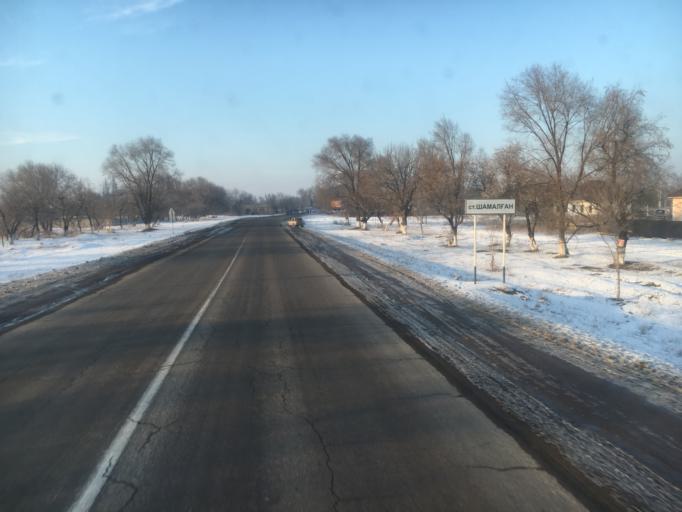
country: KZ
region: Almaty Oblysy
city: Burunday
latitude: 43.3637
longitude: 76.6424
